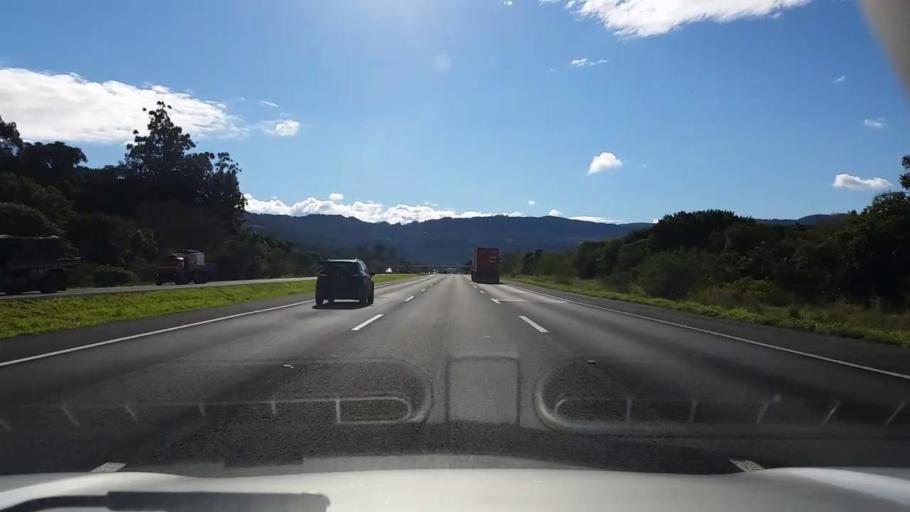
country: BR
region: Rio Grande do Sul
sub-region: Osorio
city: Osorio
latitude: -29.8782
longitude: -50.4294
